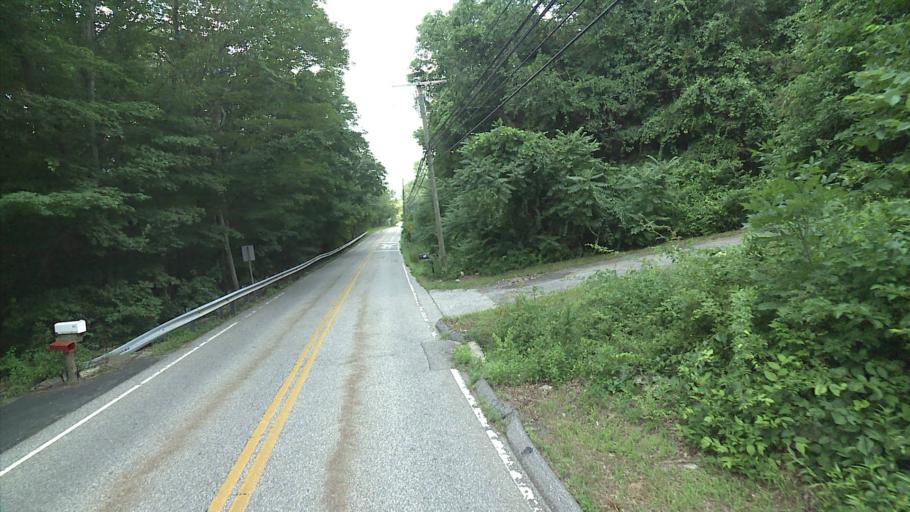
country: US
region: Connecticut
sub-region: New London County
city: Baltic
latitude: 41.6140
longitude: -72.0698
